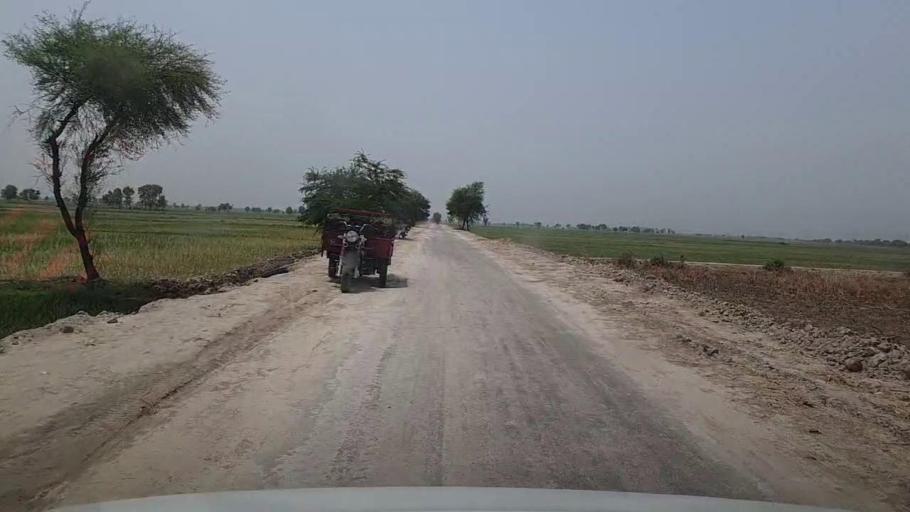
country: PK
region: Sindh
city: Sita Road
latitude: 27.0894
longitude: 67.9137
